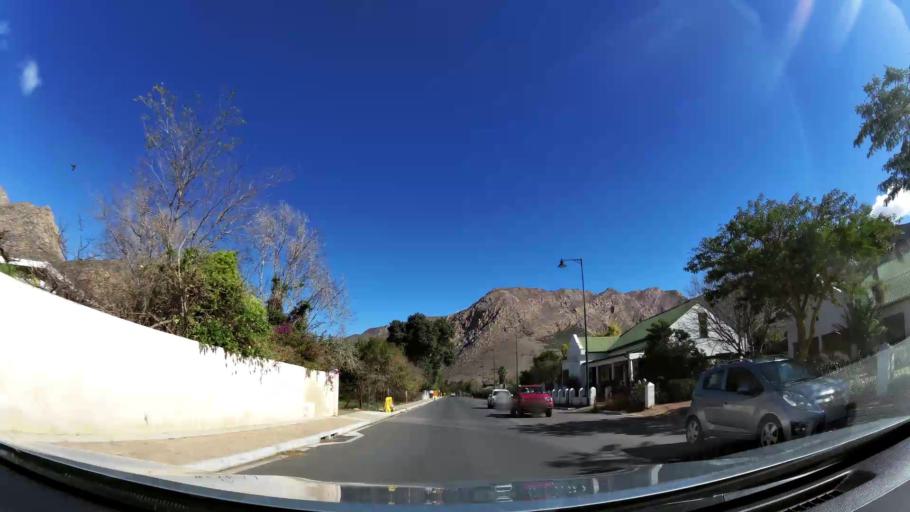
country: ZA
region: Western Cape
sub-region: Cape Winelands District Municipality
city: Ashton
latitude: -33.7903
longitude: 20.1147
